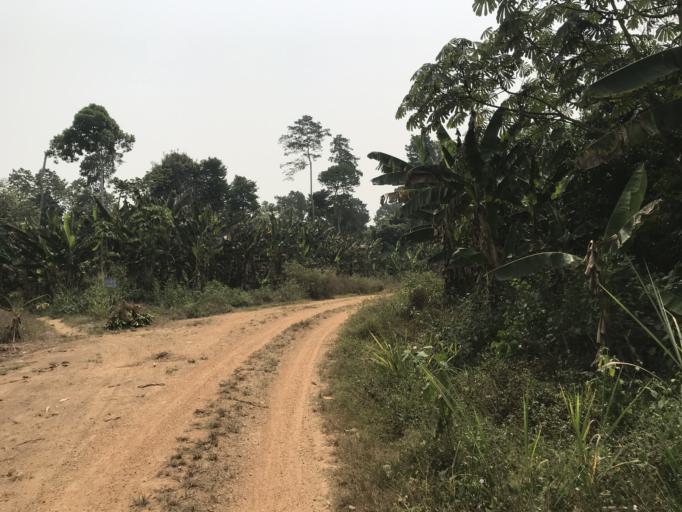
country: NG
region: Osun
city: Ifetedo
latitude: 7.0388
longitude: 4.4793
